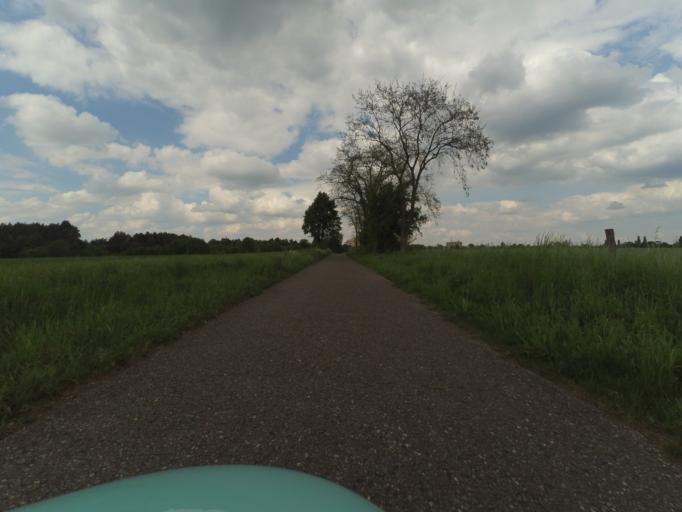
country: DE
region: Lower Saxony
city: Burgdorf
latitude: 52.4303
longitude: 10.0070
